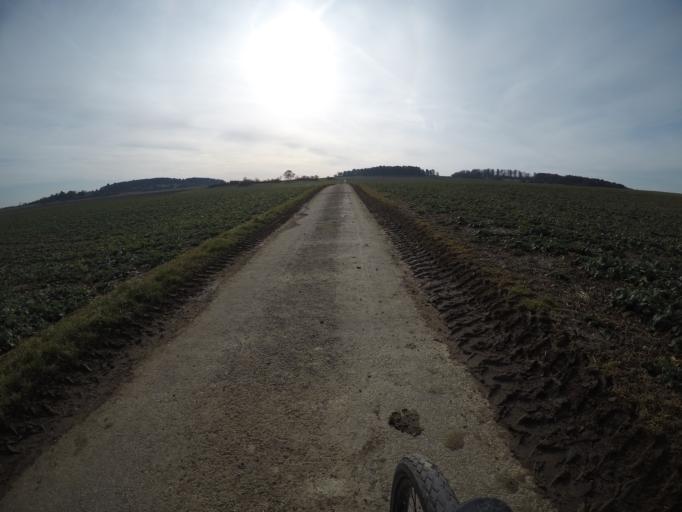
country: DE
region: Baden-Wuerttemberg
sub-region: Karlsruhe Region
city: Ostelsheim
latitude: 48.7039
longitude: 8.8653
